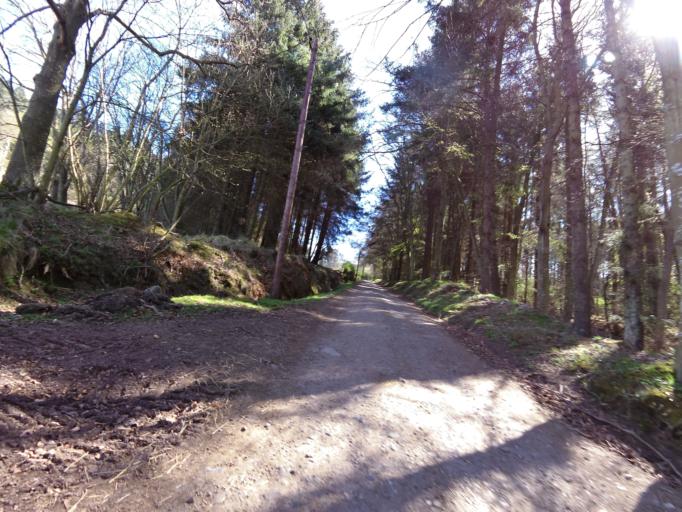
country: GB
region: Scotland
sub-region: Fife
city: Cupar
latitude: 56.3917
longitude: -3.0690
